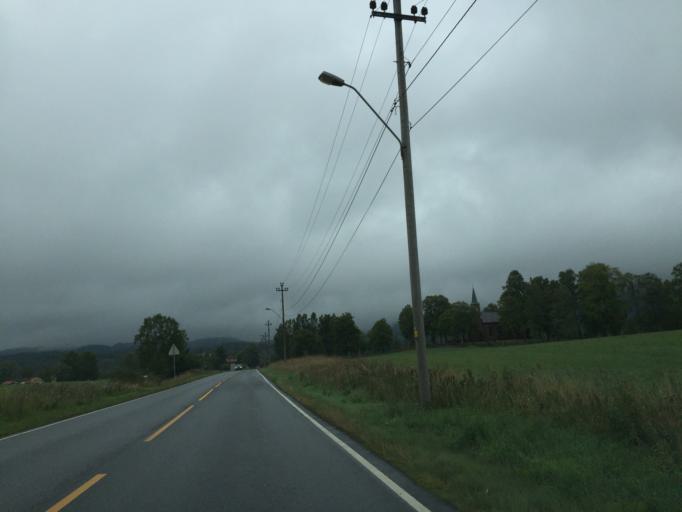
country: NO
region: Akershus
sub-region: Baerum
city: Lysaker
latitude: 60.0133
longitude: 10.6160
